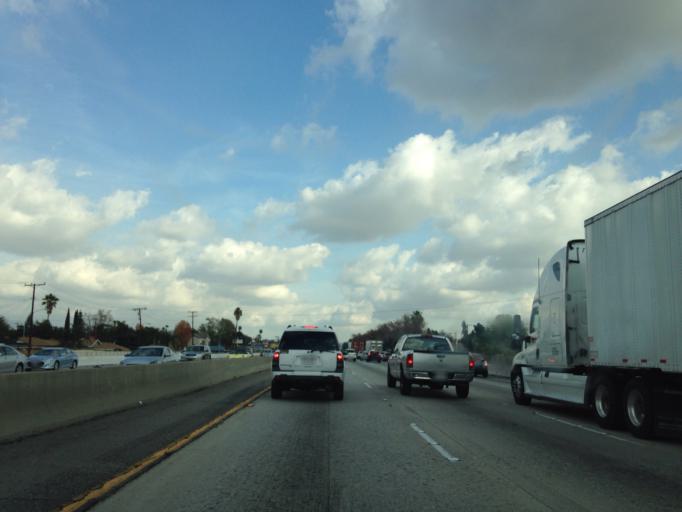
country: US
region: California
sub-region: Los Angeles County
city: Baldwin Park
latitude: 34.0709
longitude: -117.9545
